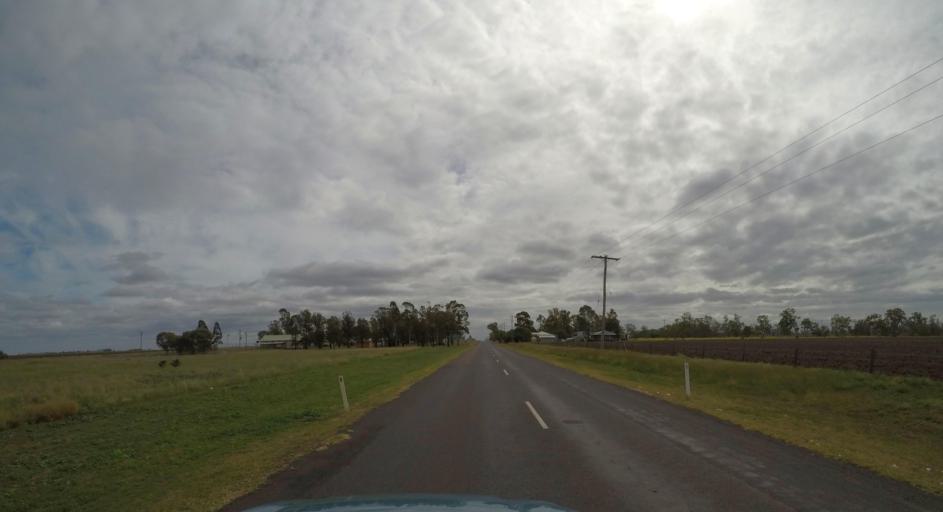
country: AU
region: Queensland
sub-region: Western Downs
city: Dalby
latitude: -26.9654
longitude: 151.2179
